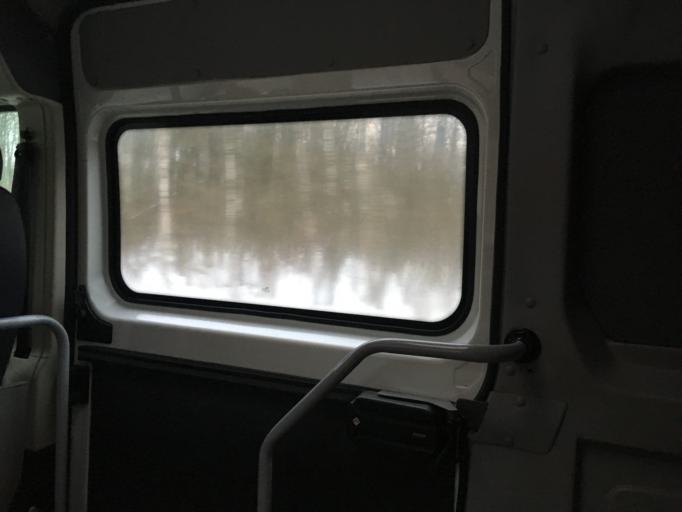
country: RU
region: Tula
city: Krapivna
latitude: 54.1288
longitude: 37.2512
